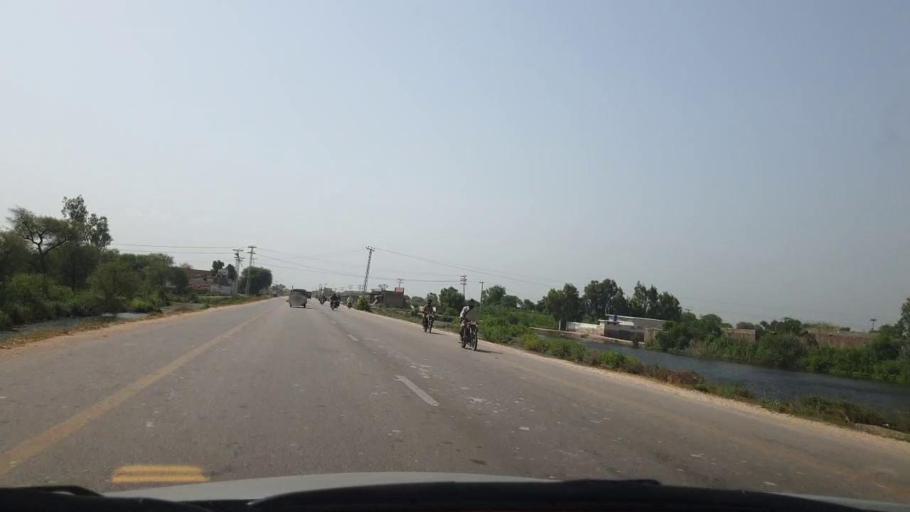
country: PK
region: Sindh
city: Matli
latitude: 25.0277
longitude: 68.6532
